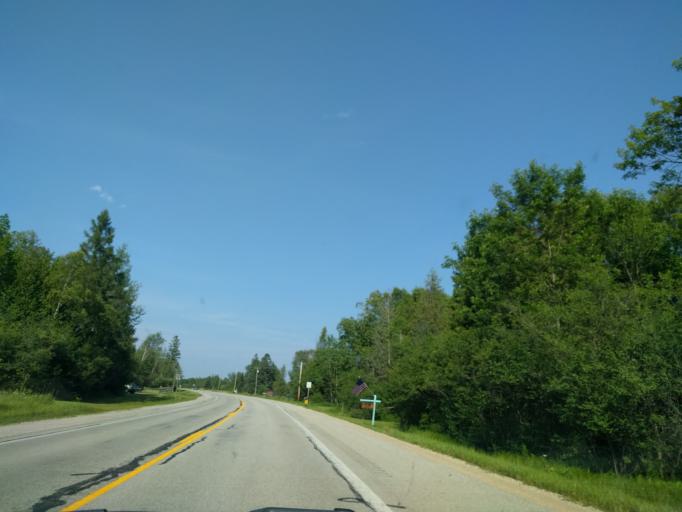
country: US
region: Michigan
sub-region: Delta County
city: Escanaba
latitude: 45.6702
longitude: -87.1550
